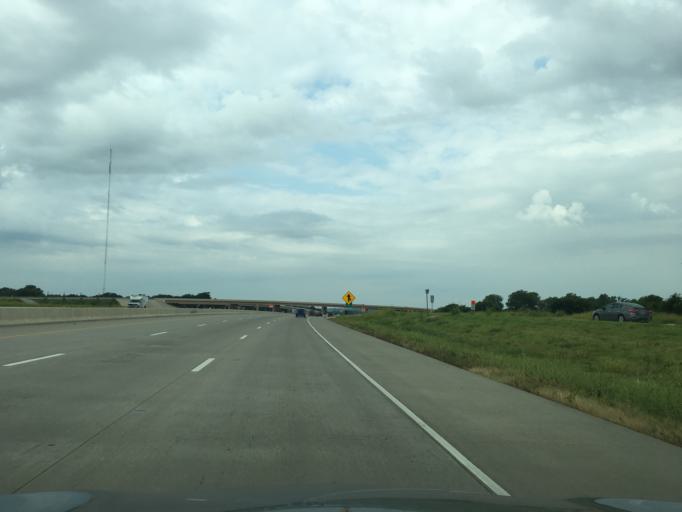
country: US
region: Texas
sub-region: Collin County
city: Melissa
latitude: 33.2679
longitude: -96.5964
